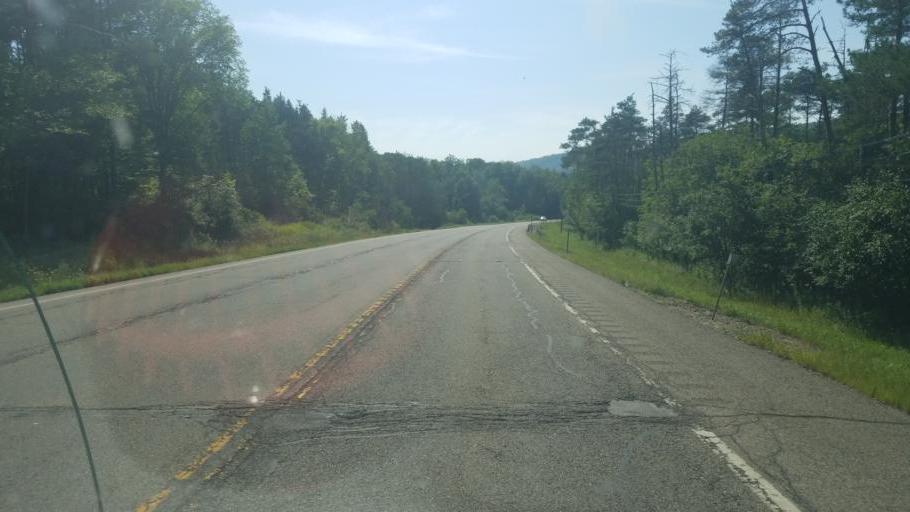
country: US
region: New York
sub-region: Allegany County
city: Wellsville
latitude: 42.1042
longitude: -78.0270
